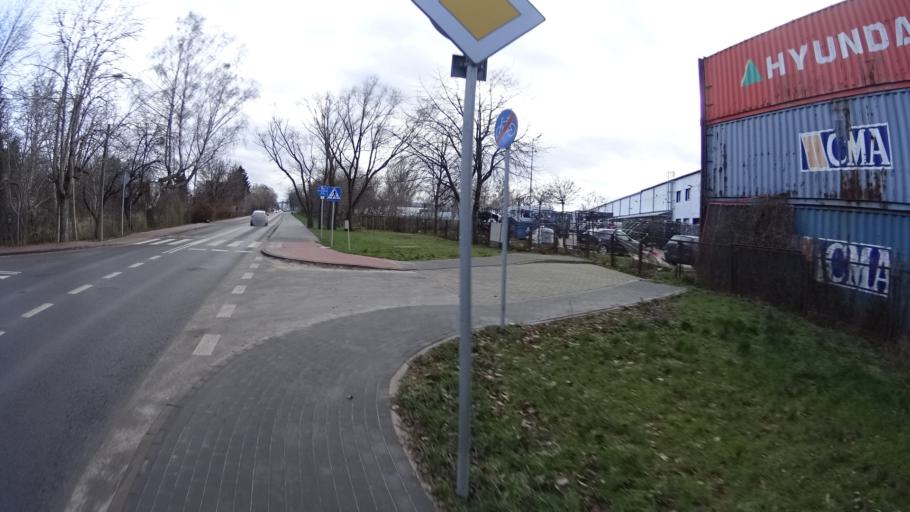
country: PL
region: Masovian Voivodeship
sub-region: Powiat pruszkowski
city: Pruszkow
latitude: 52.1678
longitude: 20.7767
